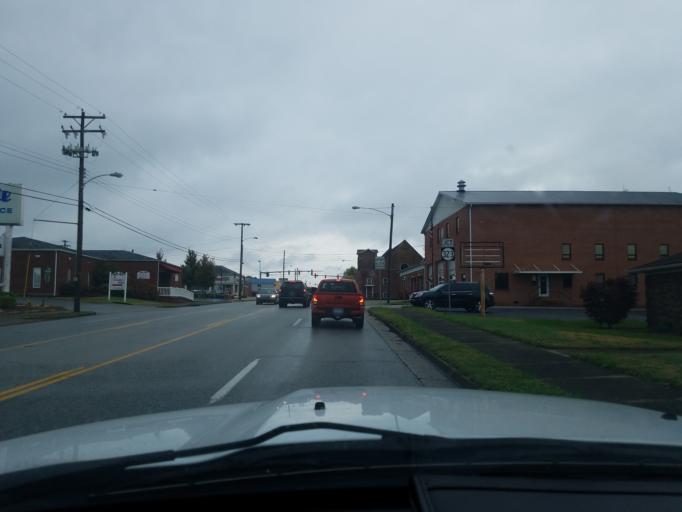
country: US
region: Kentucky
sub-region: Taylor County
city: Campbellsville
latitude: 37.3409
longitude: -85.3471
